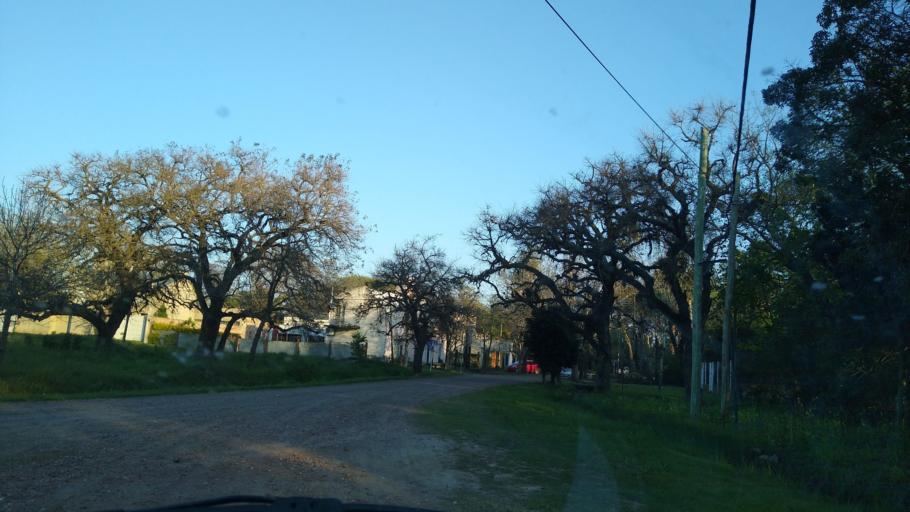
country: AR
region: Chaco
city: Barranqueras
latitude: -27.4681
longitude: -58.9547
